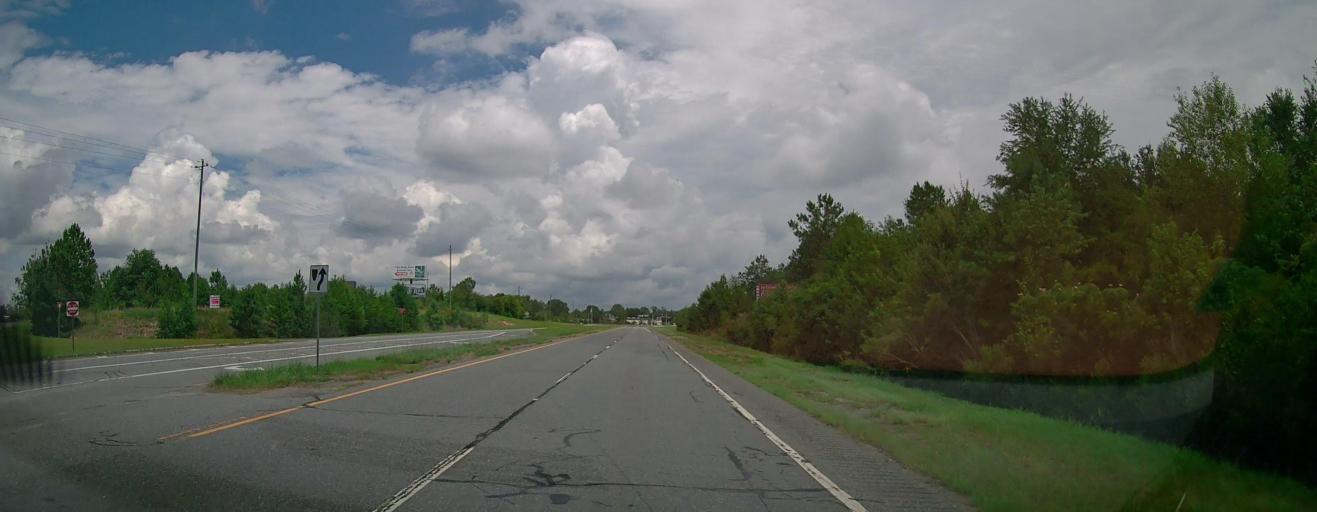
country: US
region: Georgia
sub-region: Dodge County
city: Eastman
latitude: 32.1757
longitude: -83.1684
